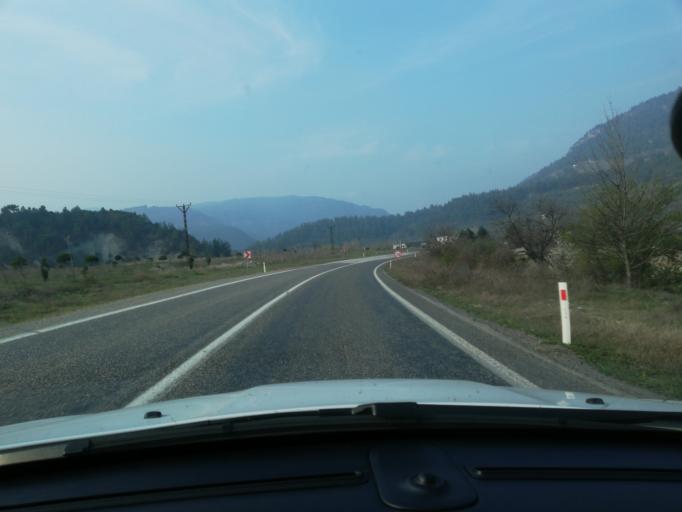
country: TR
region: Karabuk
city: Karabuk
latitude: 41.1738
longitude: 32.5844
